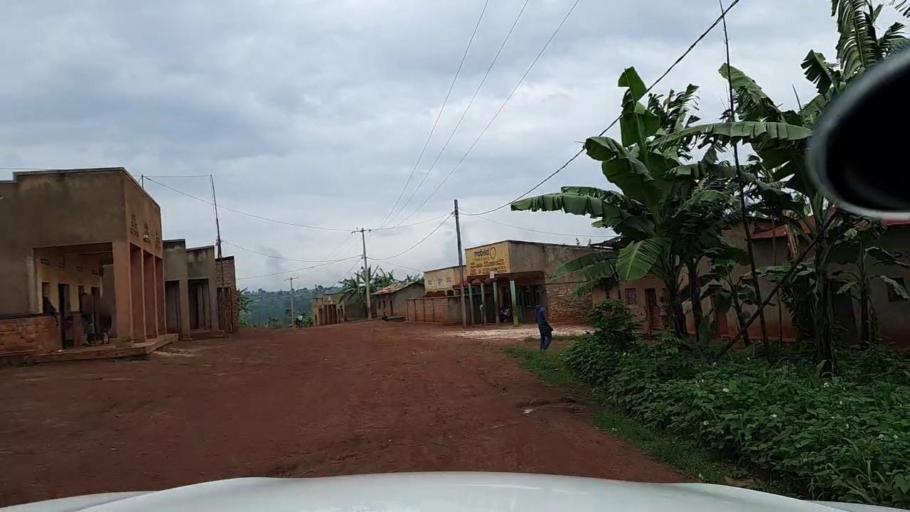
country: RW
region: Kigali
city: Kigali
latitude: -1.9121
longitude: 29.8984
